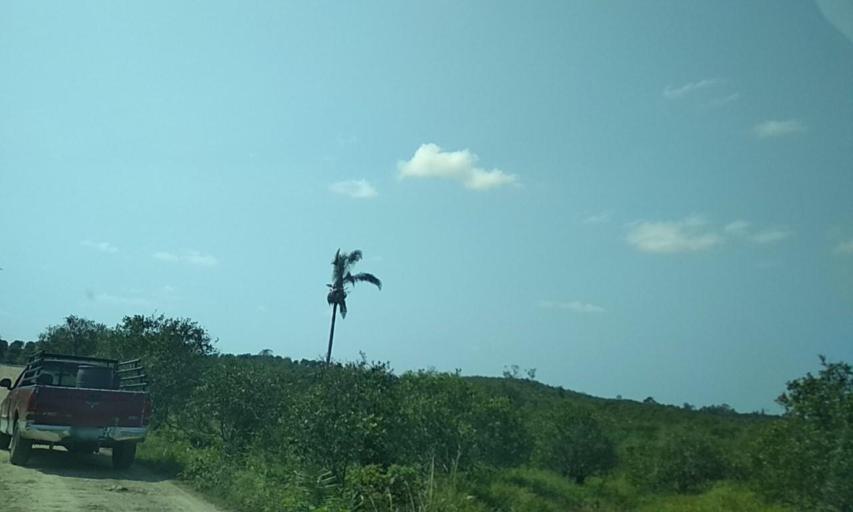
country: MX
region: Veracruz
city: Gutierrez Zamora
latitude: 20.3696
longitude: -97.1489
